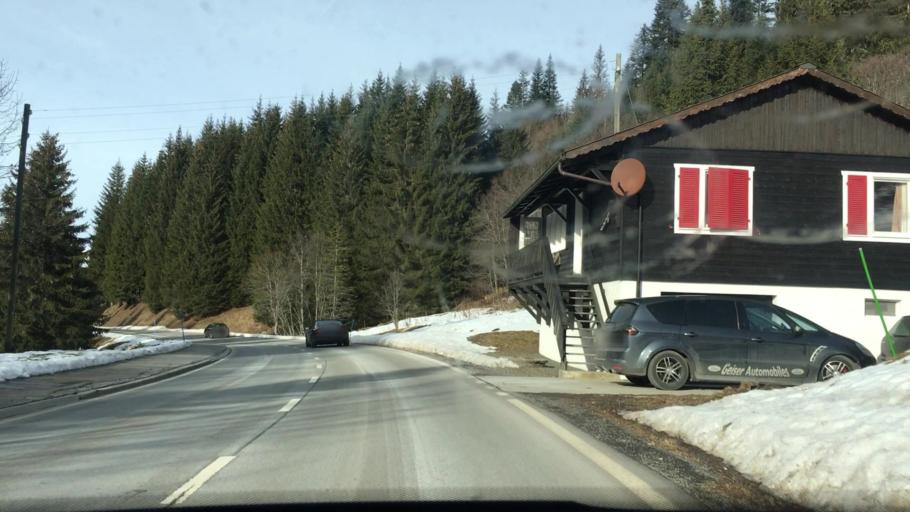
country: FR
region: Rhone-Alpes
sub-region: Departement de la Haute-Savoie
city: Chatel
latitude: 46.2464
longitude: 6.8498
